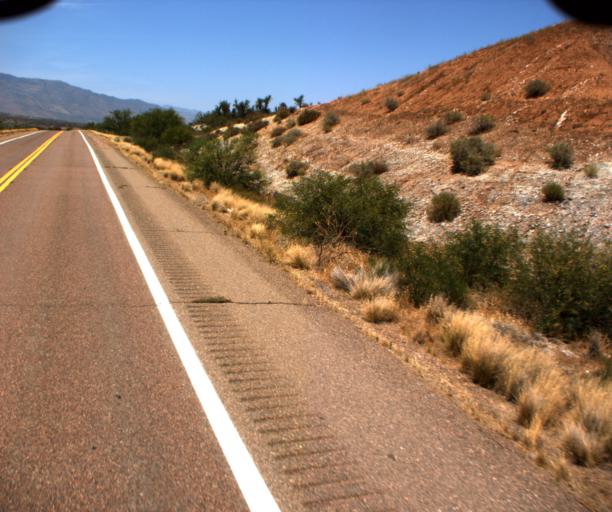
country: US
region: Arizona
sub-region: Gila County
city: Tonto Basin
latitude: 33.8066
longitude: -111.2815
